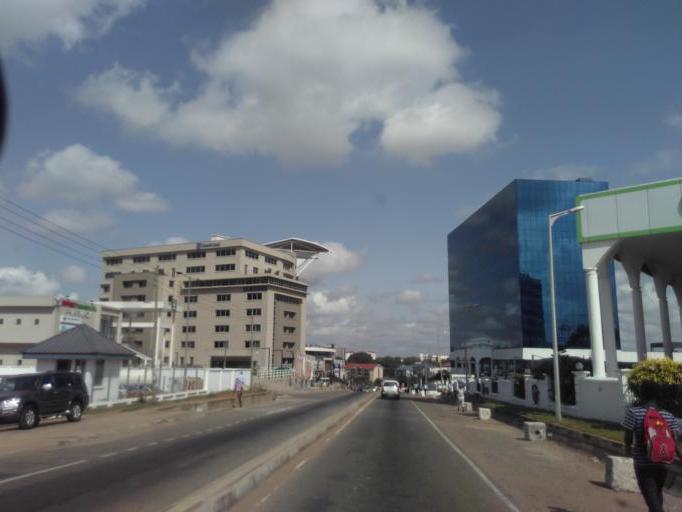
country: GH
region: Greater Accra
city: Accra
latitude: 5.5993
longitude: -0.1761
